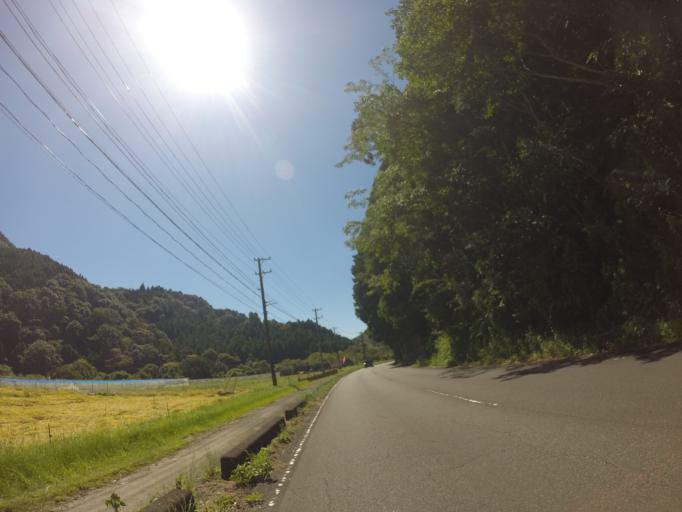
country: JP
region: Shizuoka
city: Fujieda
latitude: 34.9510
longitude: 138.2118
